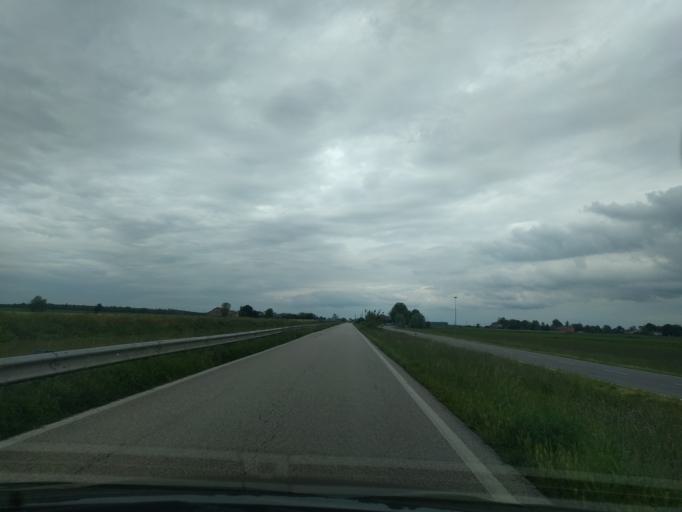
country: IT
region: Veneto
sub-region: Provincia di Rovigo
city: Mardimago
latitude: 45.0942
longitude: 11.8408
